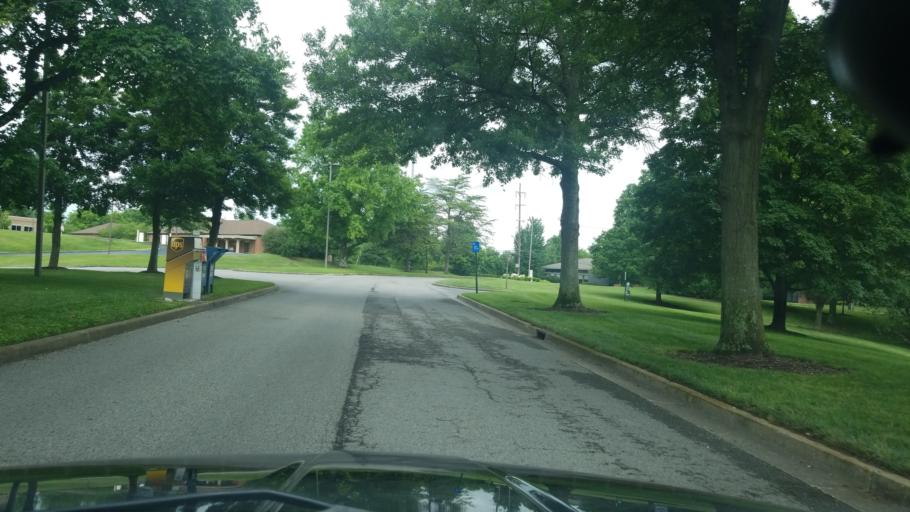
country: US
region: Tennessee
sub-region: Davidson County
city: Oak Hill
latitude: 36.0866
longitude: -86.7520
